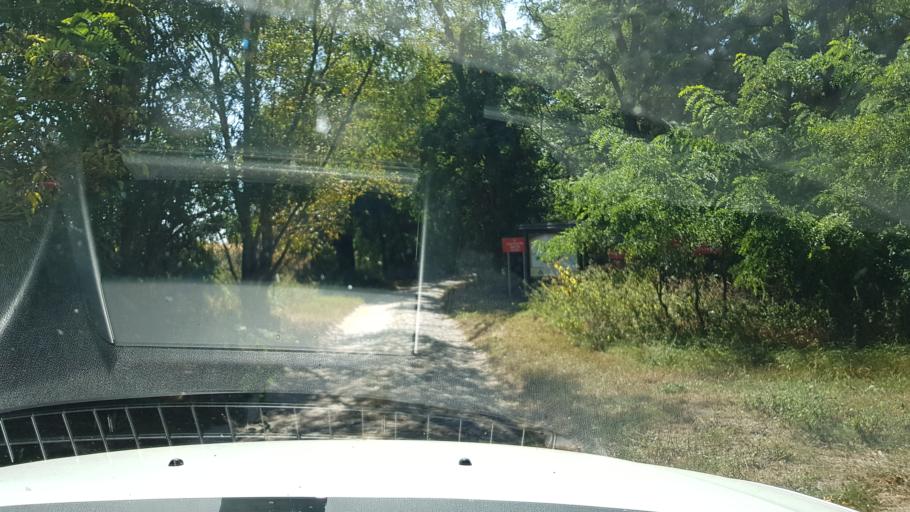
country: PL
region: West Pomeranian Voivodeship
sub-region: Powiat gryfinski
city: Cedynia
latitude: 52.8522
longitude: 14.2477
